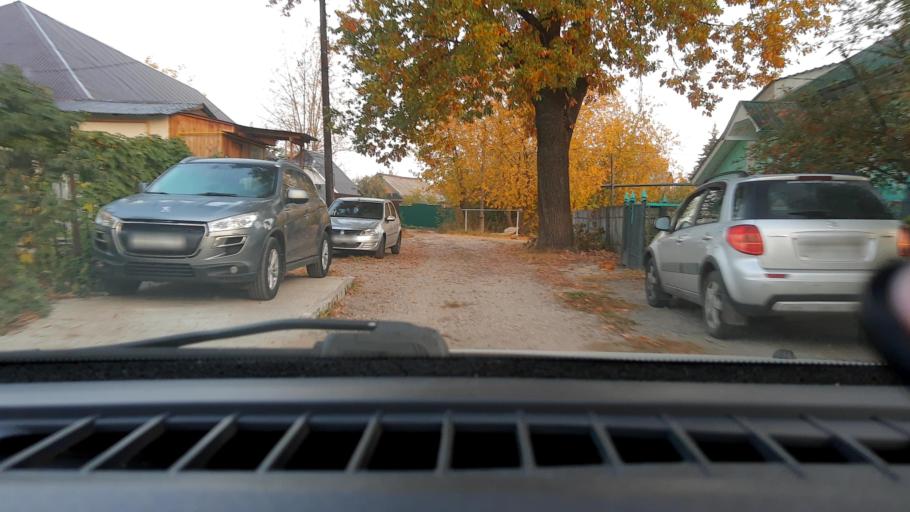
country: RU
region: Nizjnij Novgorod
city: Gorbatovka
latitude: 56.3693
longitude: 43.8194
